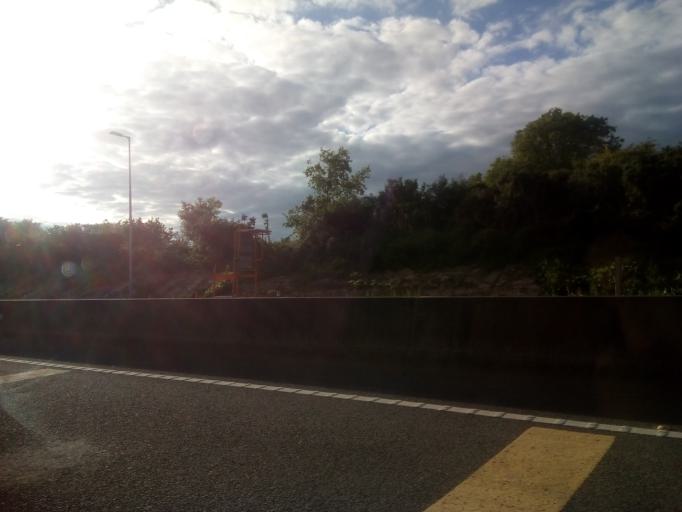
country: IE
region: Leinster
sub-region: Loch Garman
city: Gorey
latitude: 52.6497
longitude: -6.3386
